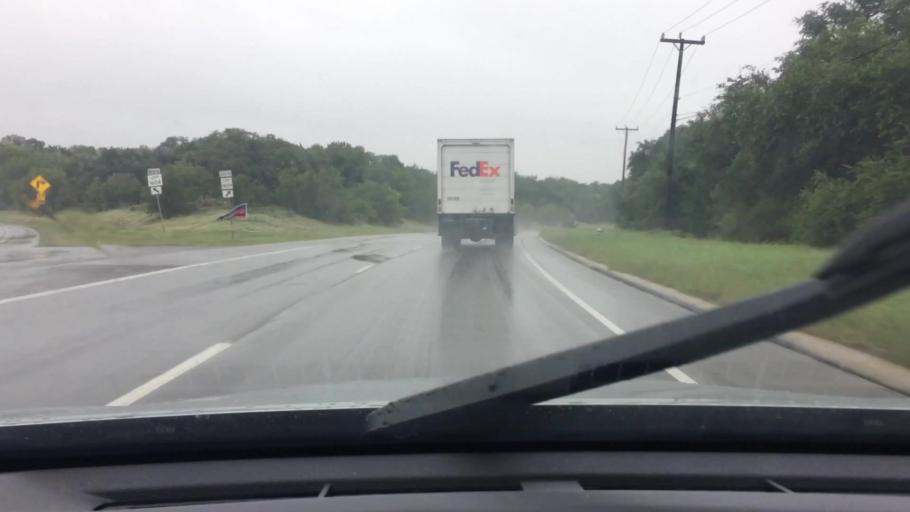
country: US
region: Texas
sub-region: Bexar County
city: Leon Valley
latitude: 29.4833
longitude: -98.7076
